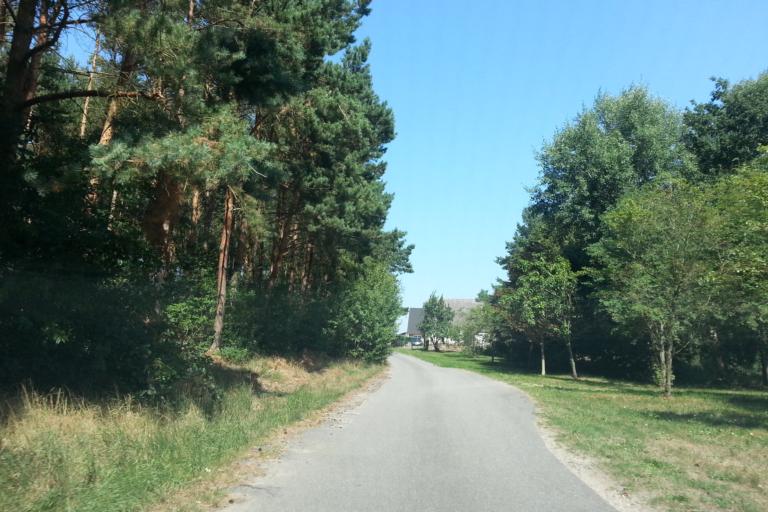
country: DE
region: Mecklenburg-Vorpommern
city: Ferdinandshof
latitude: 53.7064
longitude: 13.8366
